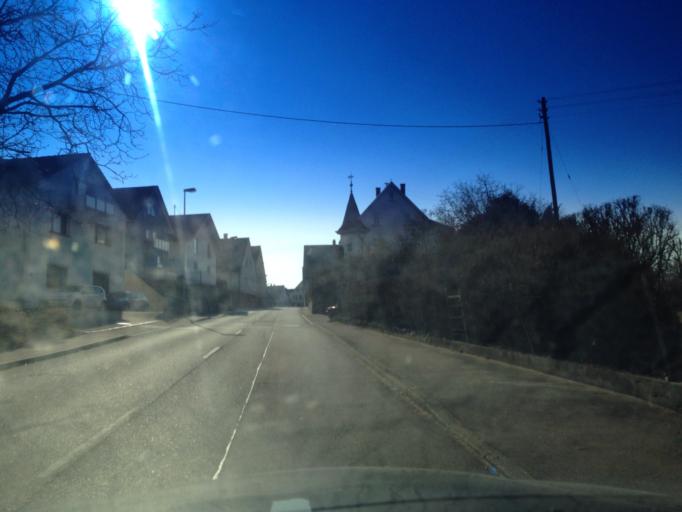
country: DE
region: Baden-Wuerttemberg
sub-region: Regierungsbezirk Stuttgart
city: Eberdingen
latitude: 48.8957
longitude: 8.9420
